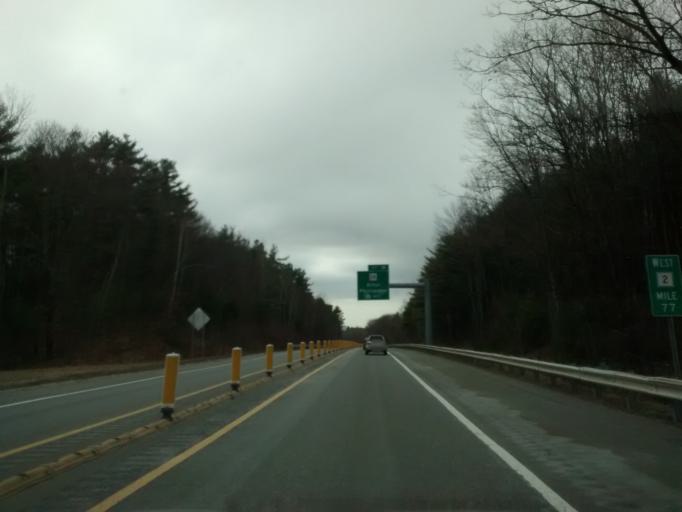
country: US
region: Massachusetts
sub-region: Worcester County
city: Phillipston
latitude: 42.5757
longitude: -72.1669
